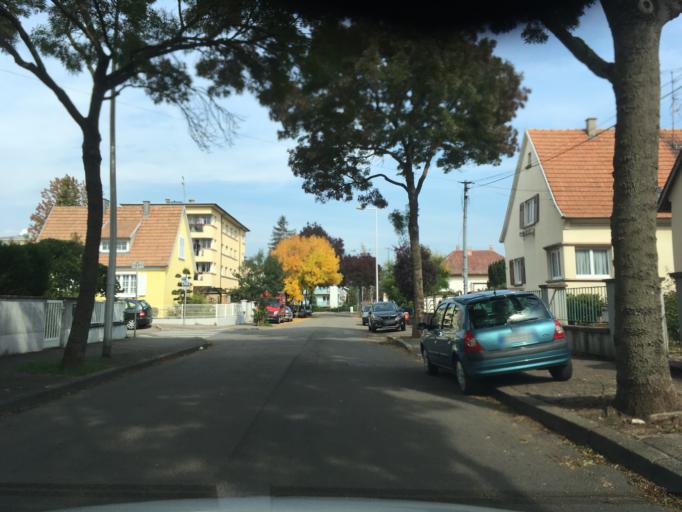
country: FR
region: Alsace
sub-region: Departement du Haut-Rhin
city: Colmar
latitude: 48.0843
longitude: 7.3683
